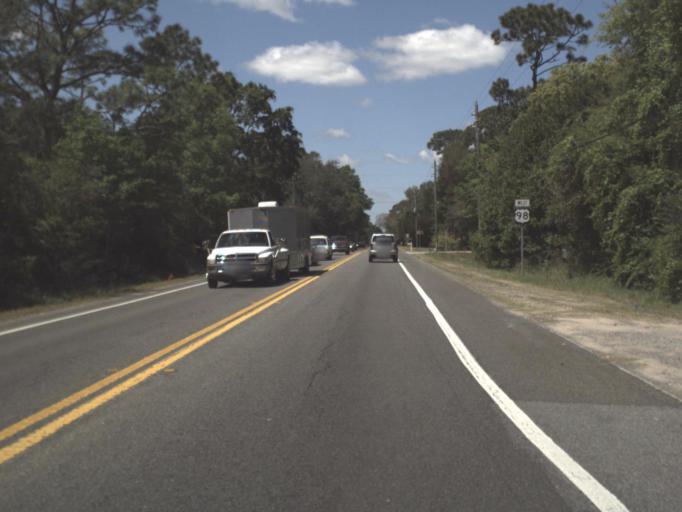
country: US
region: Florida
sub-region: Escambia County
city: Myrtle Grove
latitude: 30.3978
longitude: -87.4011
